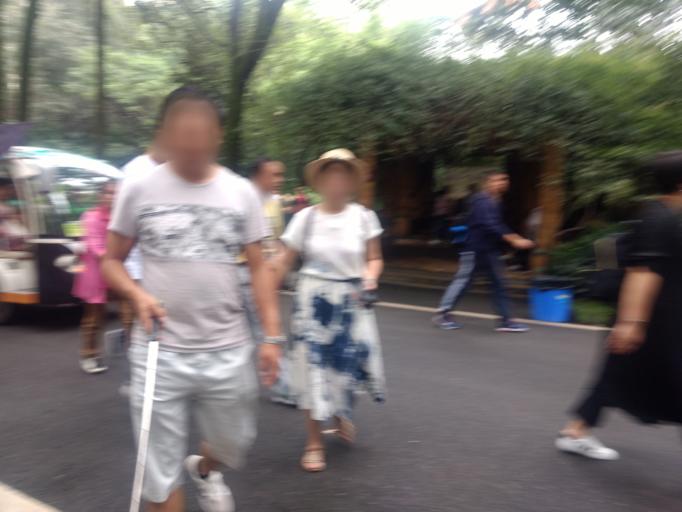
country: CN
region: Sichuan
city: Xindu
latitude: 30.7359
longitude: 104.1434
